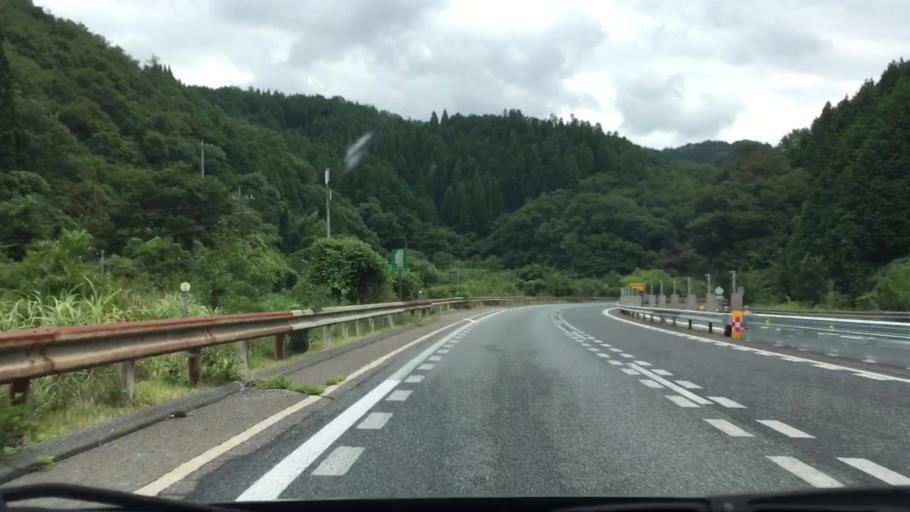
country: JP
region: Okayama
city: Niimi
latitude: 35.0205
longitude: 133.5243
